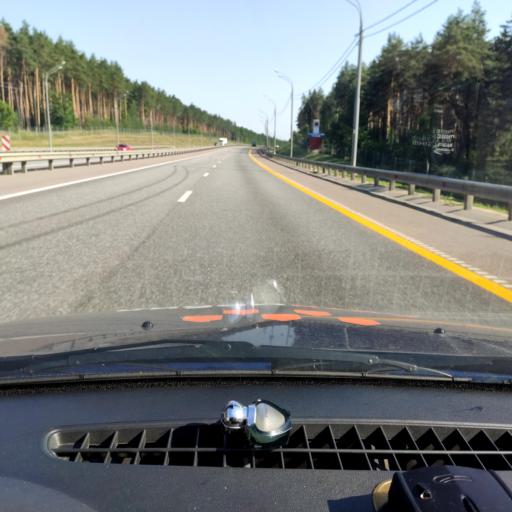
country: RU
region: Lipetsk
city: Khlevnoye
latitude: 52.3095
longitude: 39.0476
